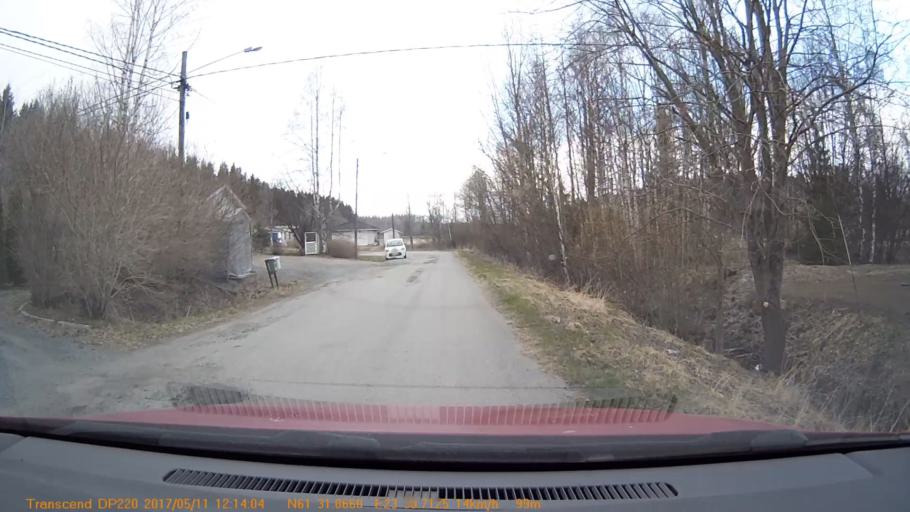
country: FI
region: Pirkanmaa
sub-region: Tampere
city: Yloejaervi
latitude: 61.5311
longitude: 23.6452
